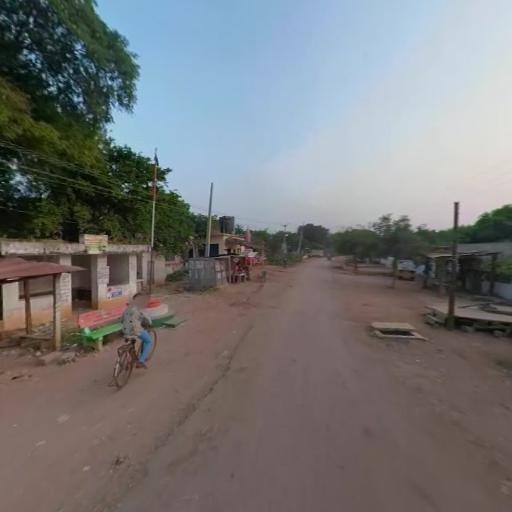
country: IN
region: Telangana
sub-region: Nalgonda
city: Suriapet
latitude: 17.0570
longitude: 79.5487
